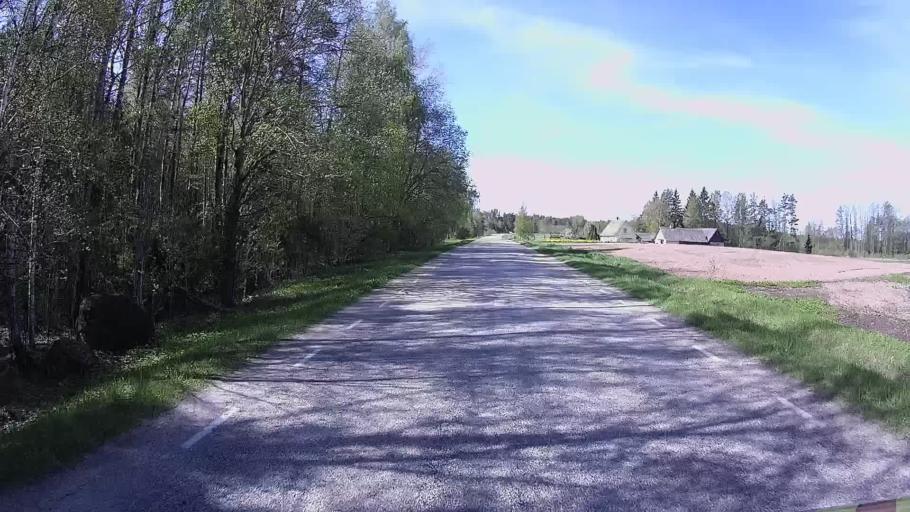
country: EE
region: Polvamaa
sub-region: Raepina vald
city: Rapina
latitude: 57.9697
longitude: 27.5523
